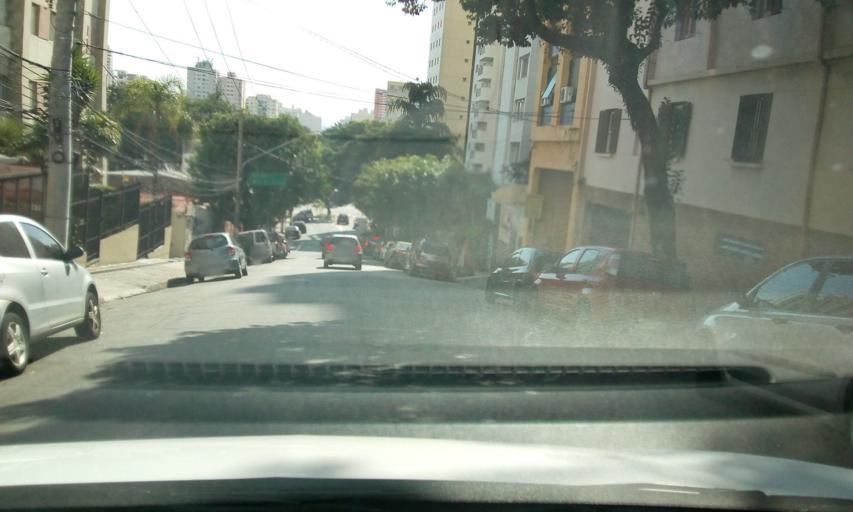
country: BR
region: Sao Paulo
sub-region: Sao Paulo
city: Sao Paulo
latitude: -23.5333
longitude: -46.6740
